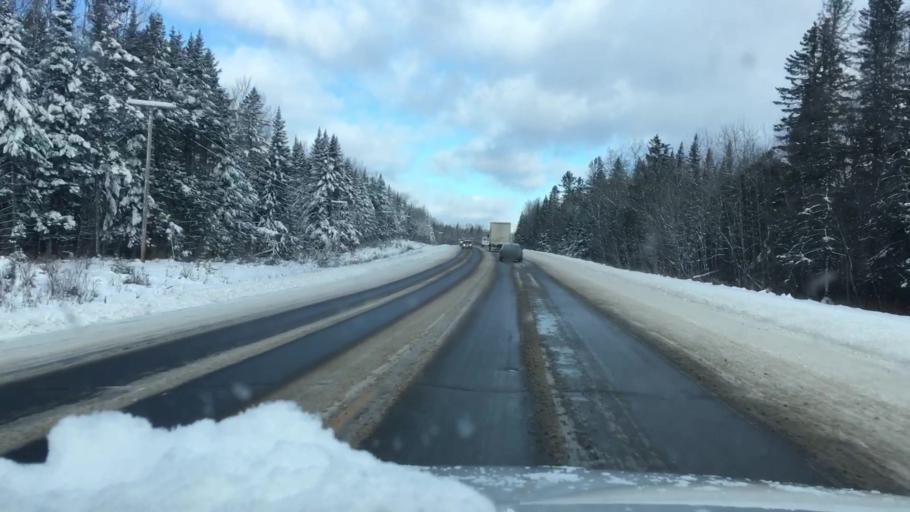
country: US
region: Maine
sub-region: Aroostook County
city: Caribou
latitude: 46.8345
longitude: -67.9976
